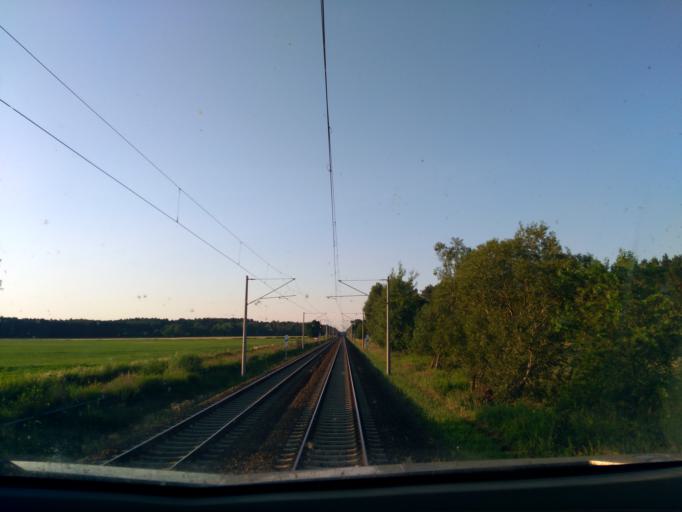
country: DE
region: Brandenburg
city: Halbe
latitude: 52.1300
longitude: 13.6789
